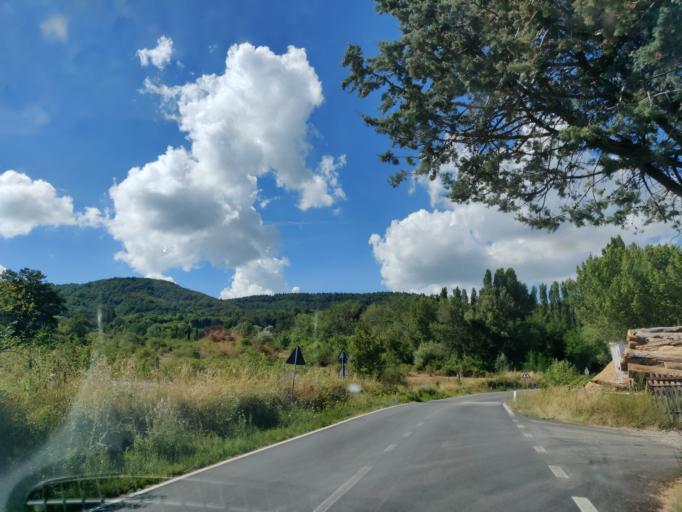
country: IT
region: Tuscany
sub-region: Provincia di Siena
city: Abbadia San Salvatore
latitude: 42.8993
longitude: 11.6677
